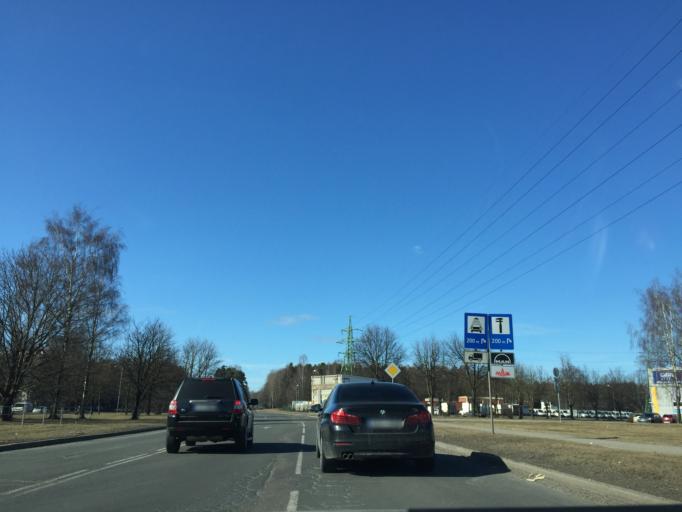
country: LV
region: Marupe
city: Marupe
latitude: 56.9646
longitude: 24.0275
